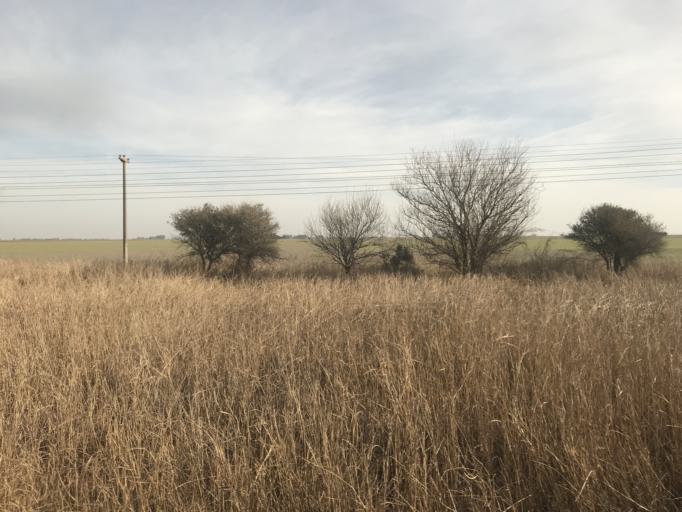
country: AR
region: Cordoba
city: Laguna Larga
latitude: -31.7599
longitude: -63.8179
